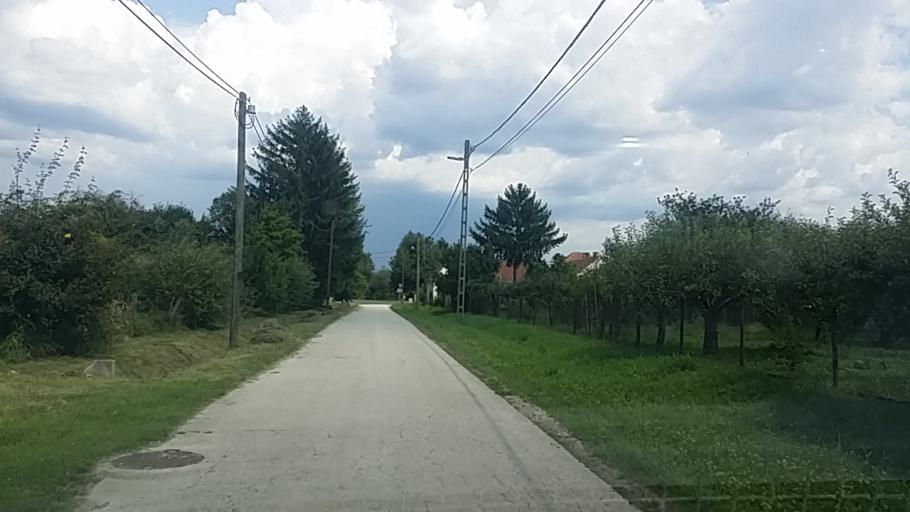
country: HR
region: Medimurska
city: Podturen
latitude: 46.5175
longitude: 16.5552
